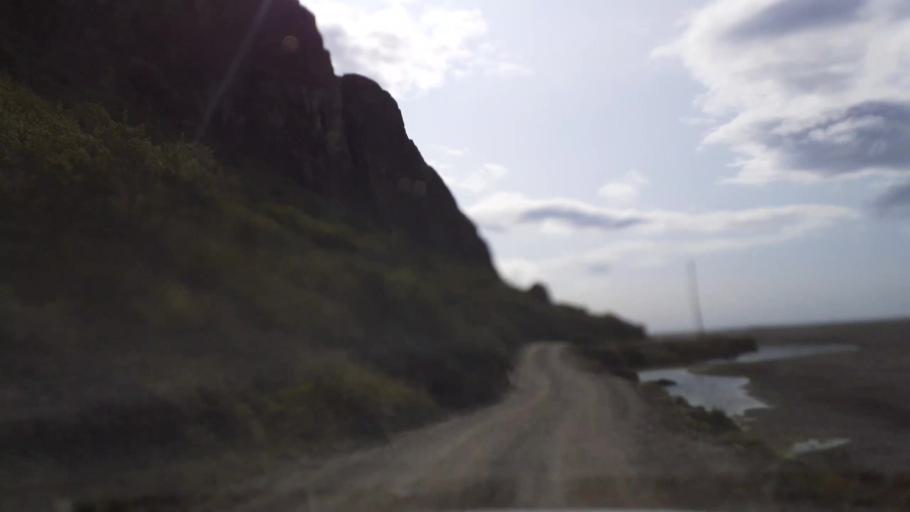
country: IS
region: East
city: Hoefn
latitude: 64.4325
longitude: -14.8917
